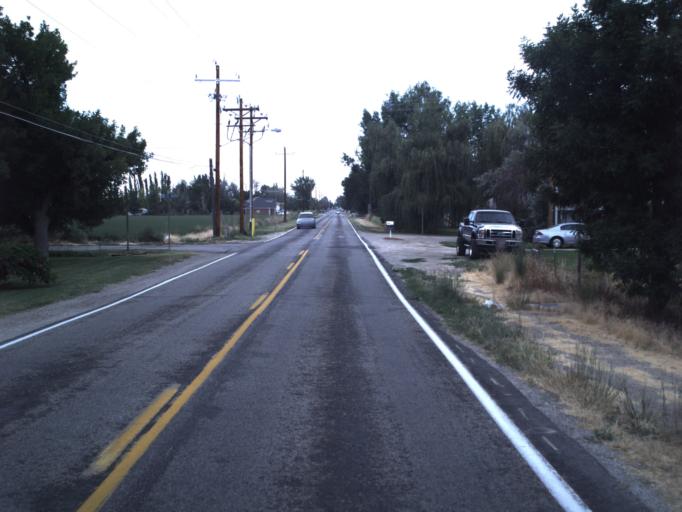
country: US
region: Utah
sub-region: Davis County
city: West Point
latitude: 41.1102
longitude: -112.1125
